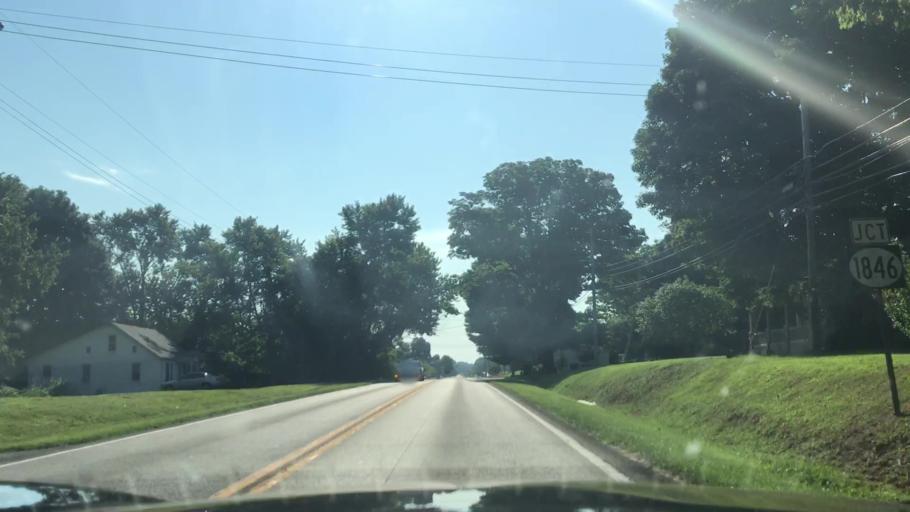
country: US
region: Kentucky
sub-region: Hart County
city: Horse Cave
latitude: 37.1784
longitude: -85.8949
